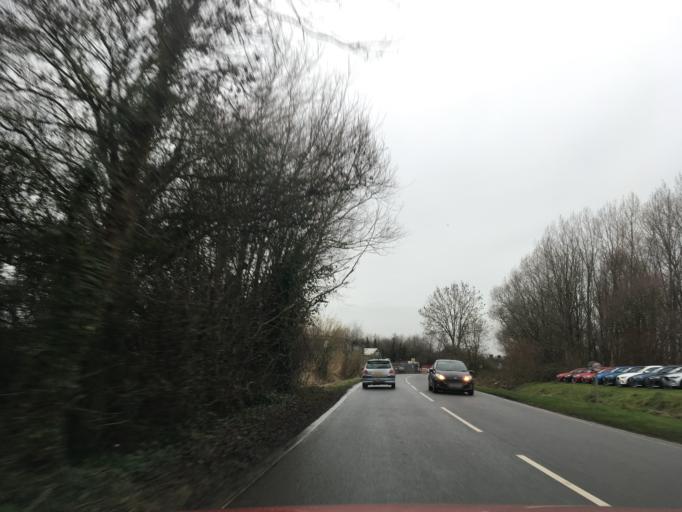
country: GB
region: Wales
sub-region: Newport
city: Nash
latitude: 51.5683
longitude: -2.9523
